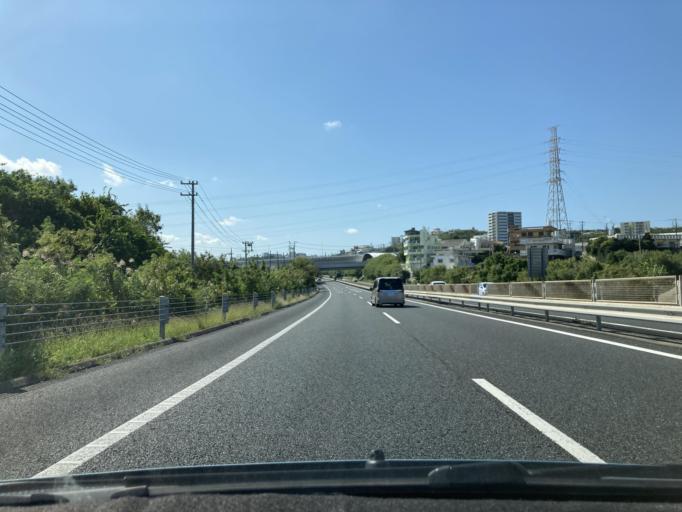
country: JP
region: Okinawa
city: Ginowan
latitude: 26.2438
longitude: 127.7450
